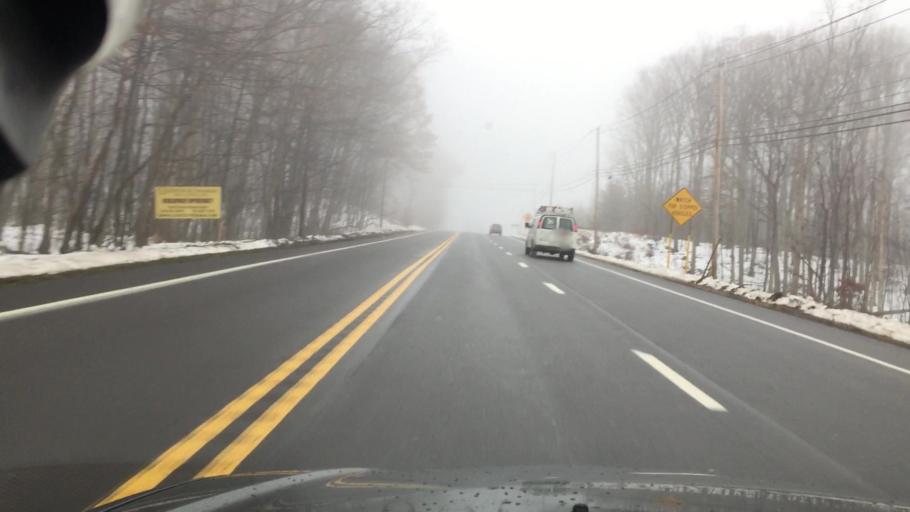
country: US
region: Pennsylvania
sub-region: Luzerne County
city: Freeland
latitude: 41.0596
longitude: -75.9625
